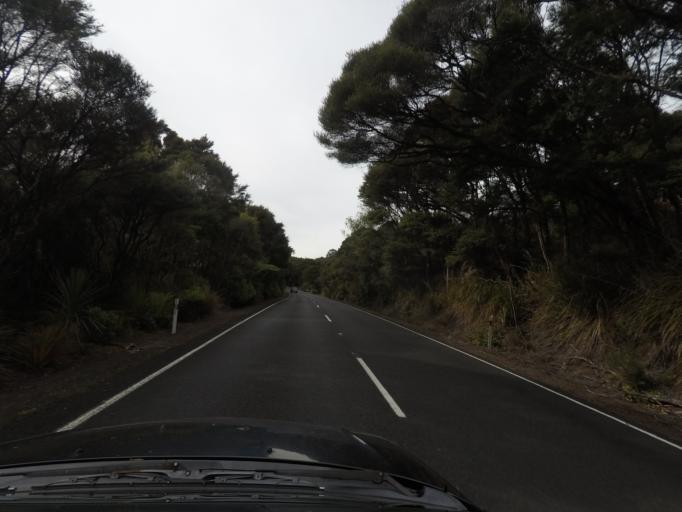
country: NZ
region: Auckland
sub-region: Auckland
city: Titirangi
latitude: -36.9340
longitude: 174.5656
